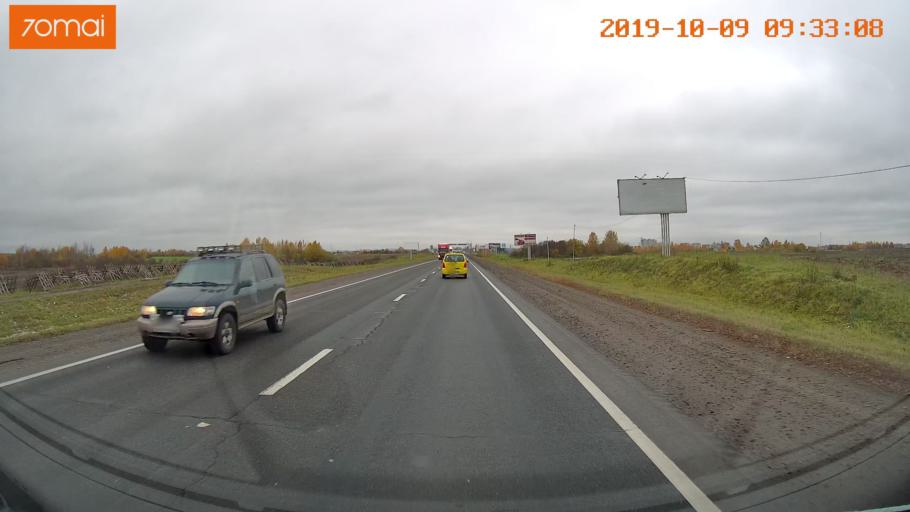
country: RU
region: Vologda
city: Vologda
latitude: 59.1656
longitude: 39.9189
